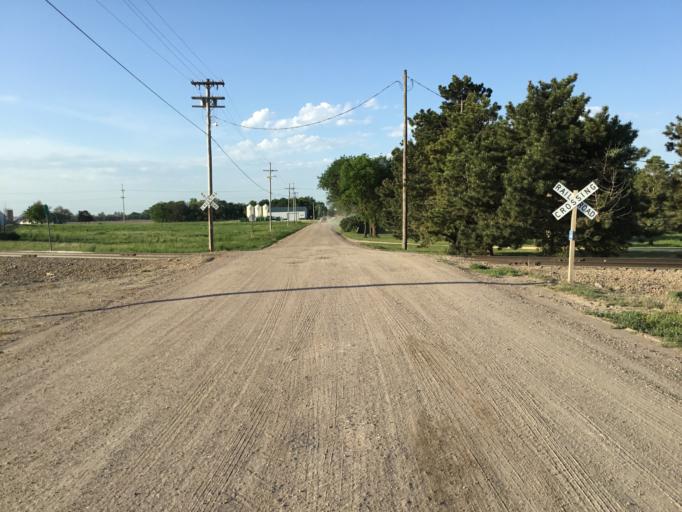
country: US
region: Kansas
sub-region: Mitchell County
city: Beloit
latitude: 39.4537
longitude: -98.0975
